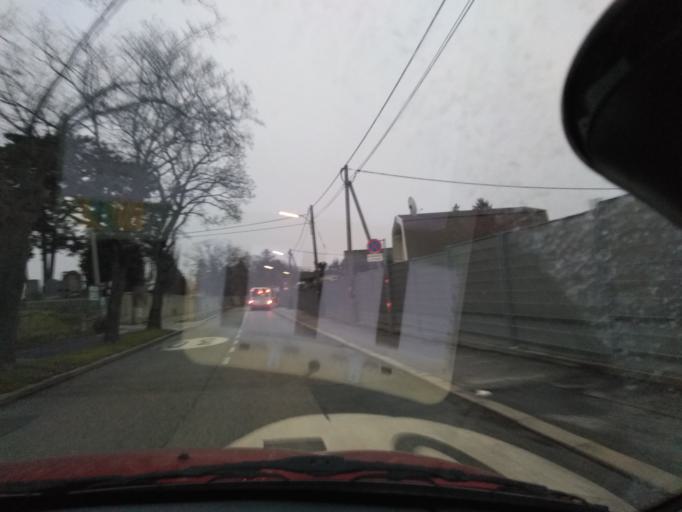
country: AT
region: Vienna
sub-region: Wien Stadt
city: Vienna
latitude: 48.2300
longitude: 16.3157
